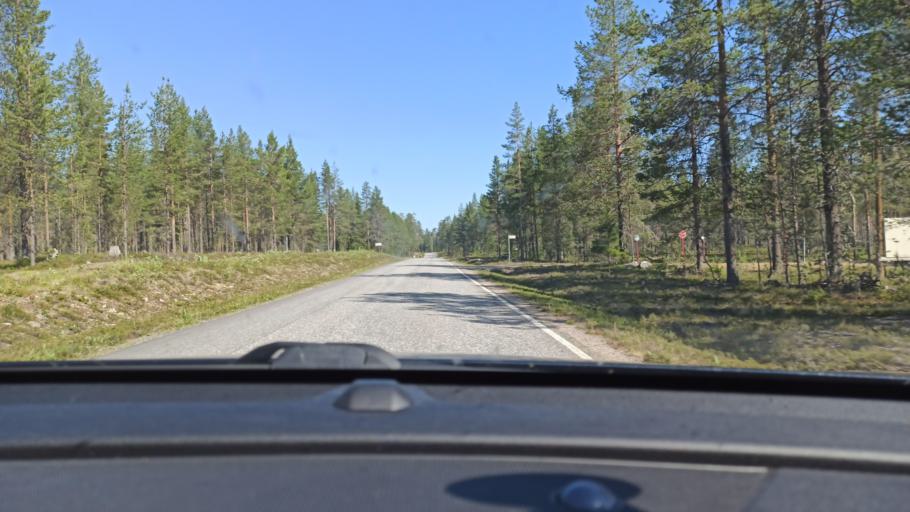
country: FI
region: Lapland
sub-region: Tunturi-Lappi
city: Kolari
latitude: 67.6556
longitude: 24.1641
